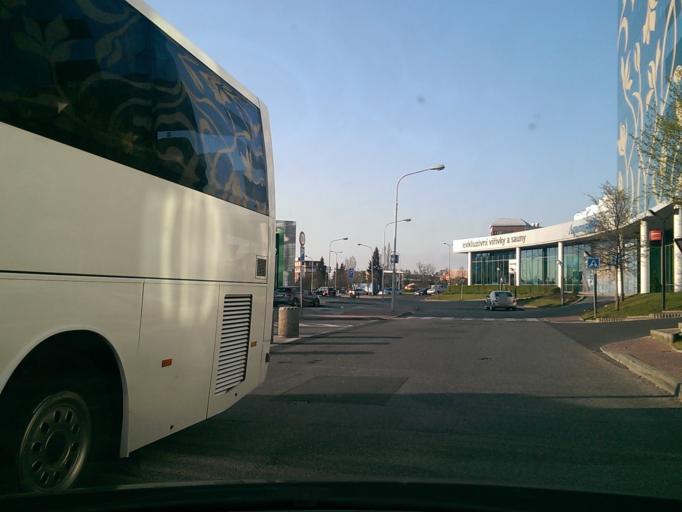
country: CZ
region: Central Bohemia
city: Vestec
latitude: 50.0366
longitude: 14.4922
